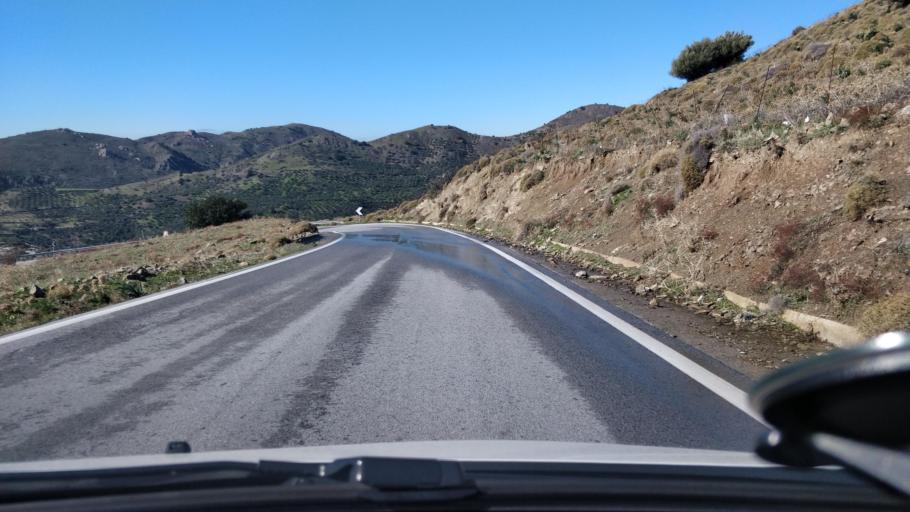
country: GR
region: Crete
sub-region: Nomos Irakleiou
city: Kastelli
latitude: 35.0366
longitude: 25.4435
